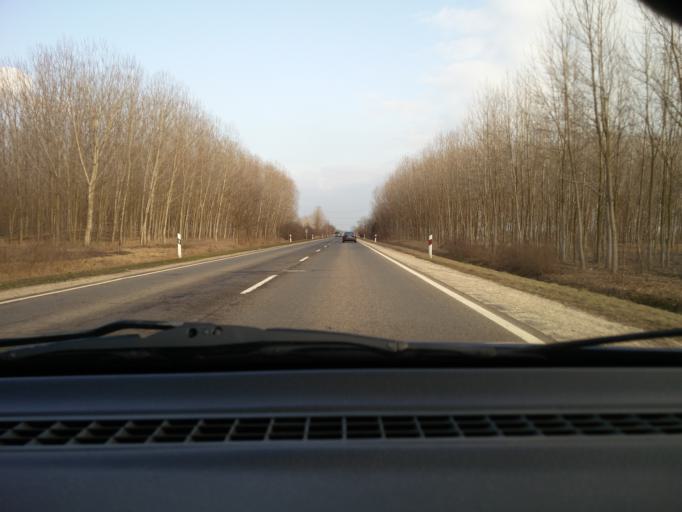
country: HU
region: Pest
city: Nyaregyhaza
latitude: 47.2485
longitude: 19.4683
